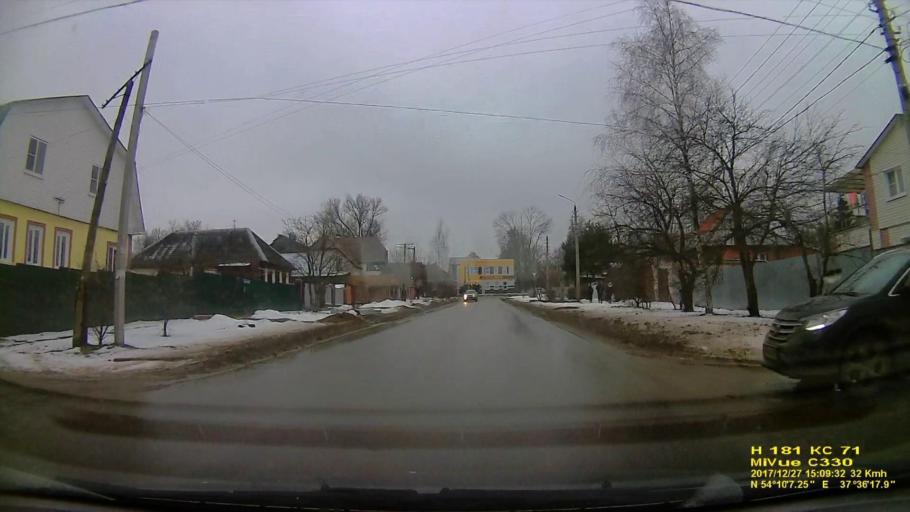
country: RU
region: Tula
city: Tula
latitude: 54.1686
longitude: 37.6049
